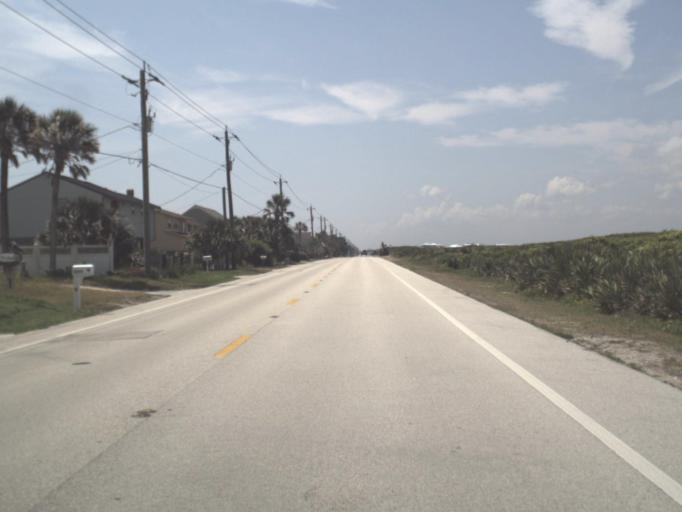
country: US
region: Florida
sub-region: Saint Johns County
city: Villano Beach
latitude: 30.0056
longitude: -81.3190
